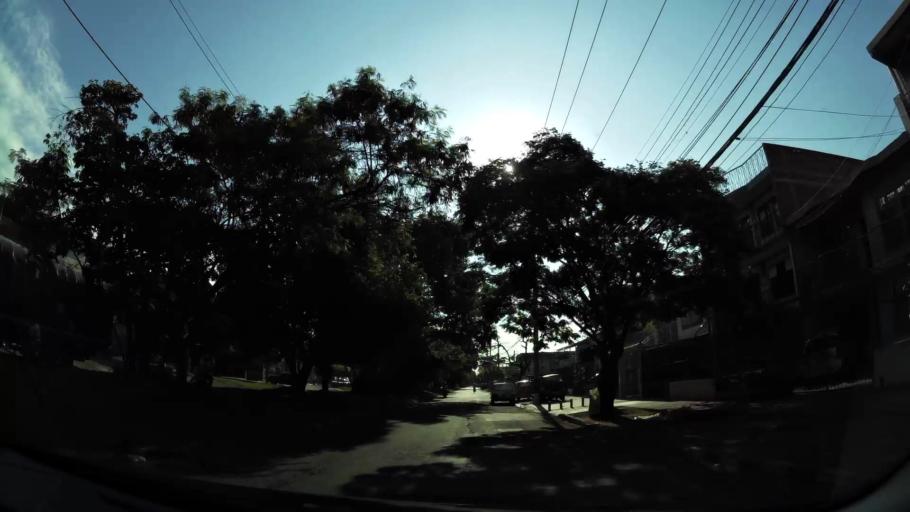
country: CO
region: Valle del Cauca
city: Cali
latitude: 3.4283
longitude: -76.5133
